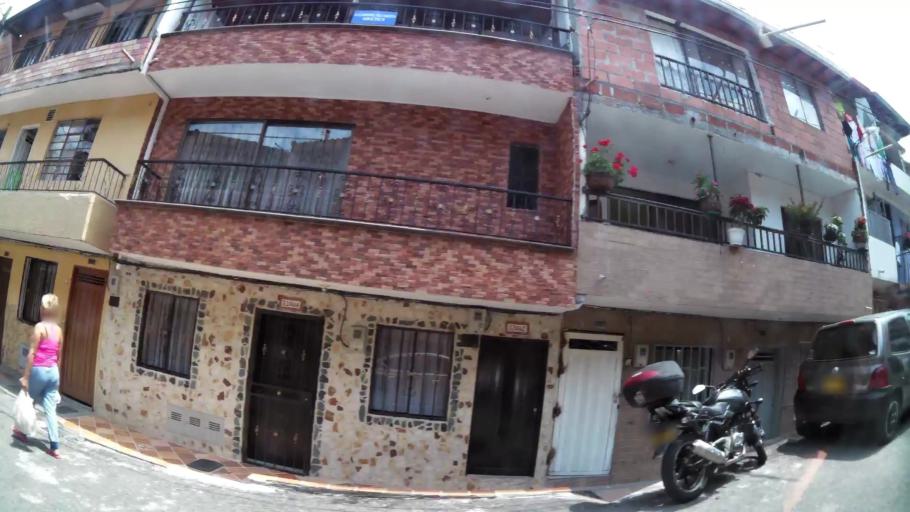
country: CO
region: Antioquia
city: Itagui
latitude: 6.1849
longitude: -75.5998
